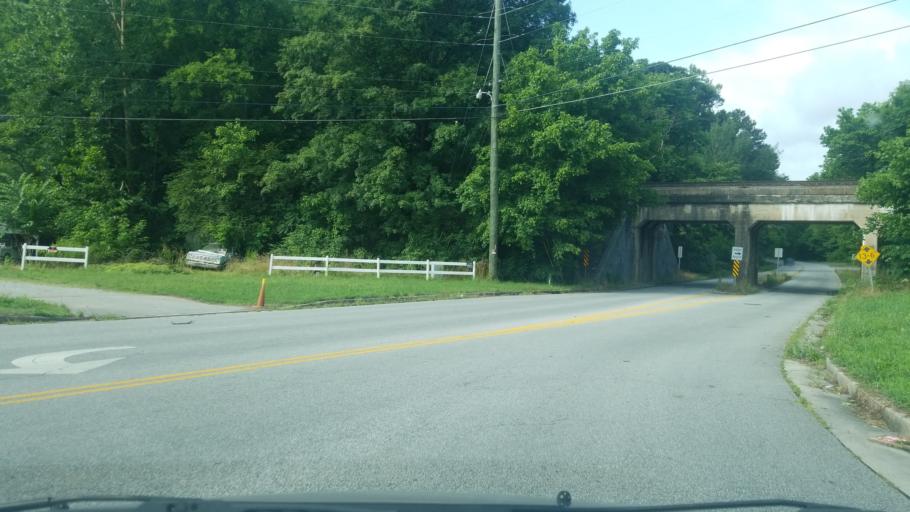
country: US
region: Tennessee
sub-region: Hamilton County
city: Apison
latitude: 35.0220
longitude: -85.0223
